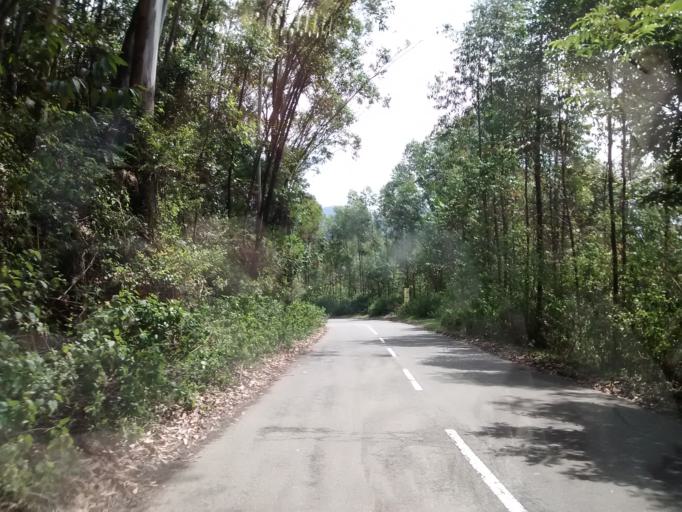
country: IN
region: Kerala
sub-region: Idukki
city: Munnar
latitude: 10.0991
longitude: 77.1140
